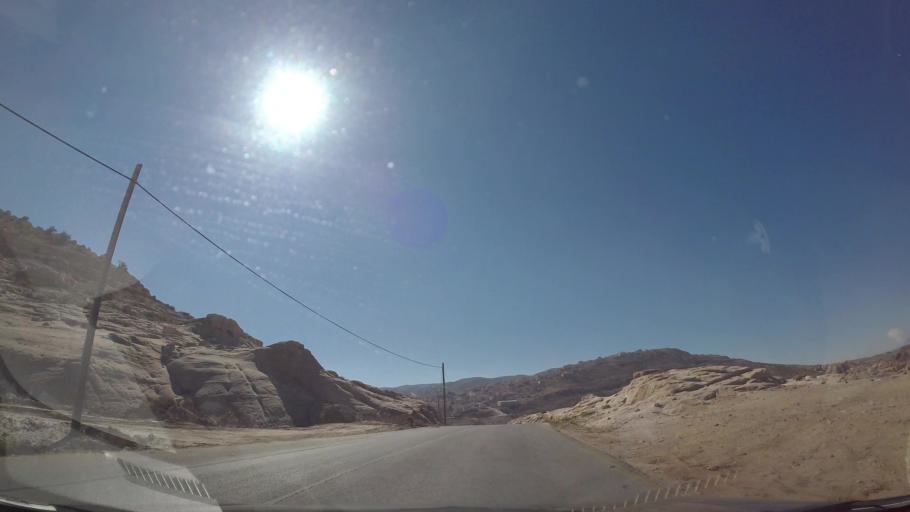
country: JO
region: Ma'an
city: Petra
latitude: 30.3312
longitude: 35.4687
